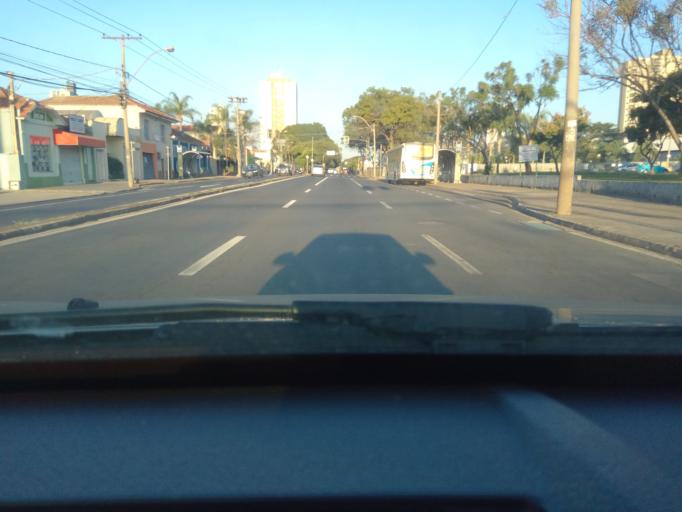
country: BR
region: Sao Paulo
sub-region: Piracicaba
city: Piracicaba
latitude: -22.7345
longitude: -47.6568
